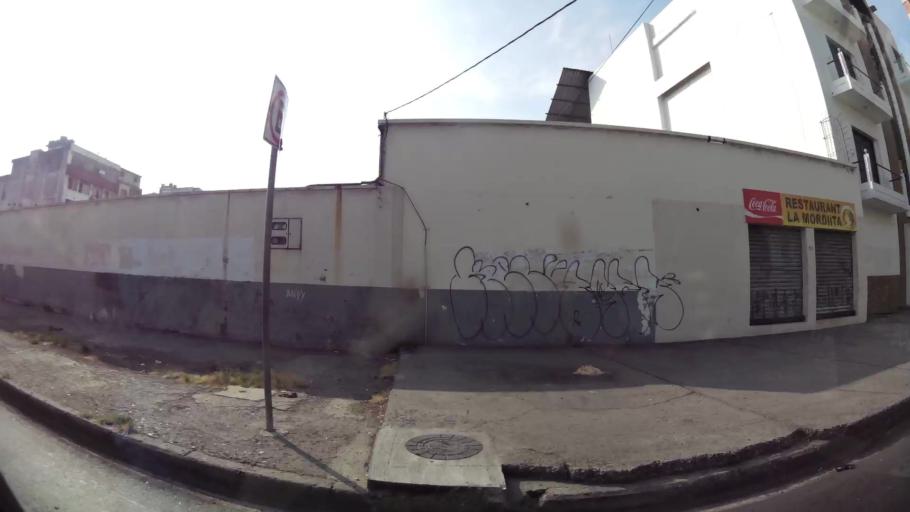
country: EC
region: Guayas
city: Eloy Alfaro
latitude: -2.1883
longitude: -79.8819
